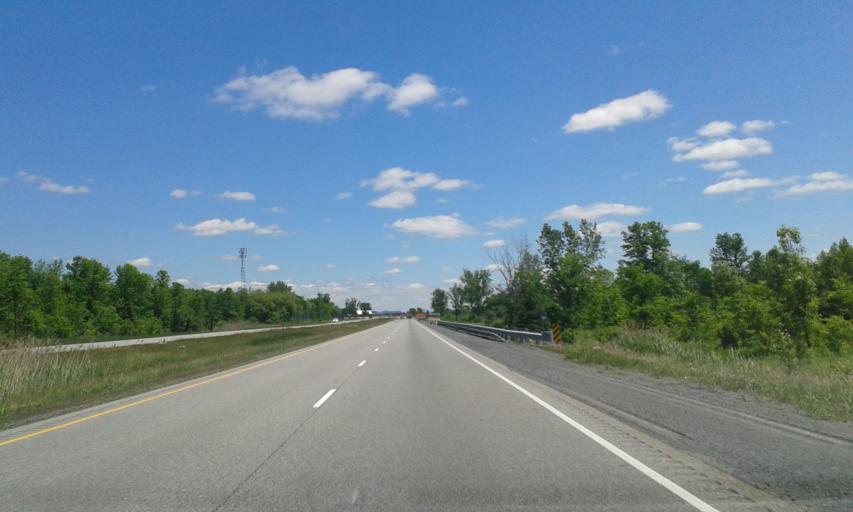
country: US
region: New York
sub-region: St. Lawrence County
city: Norfolk
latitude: 44.9594
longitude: -75.0940
